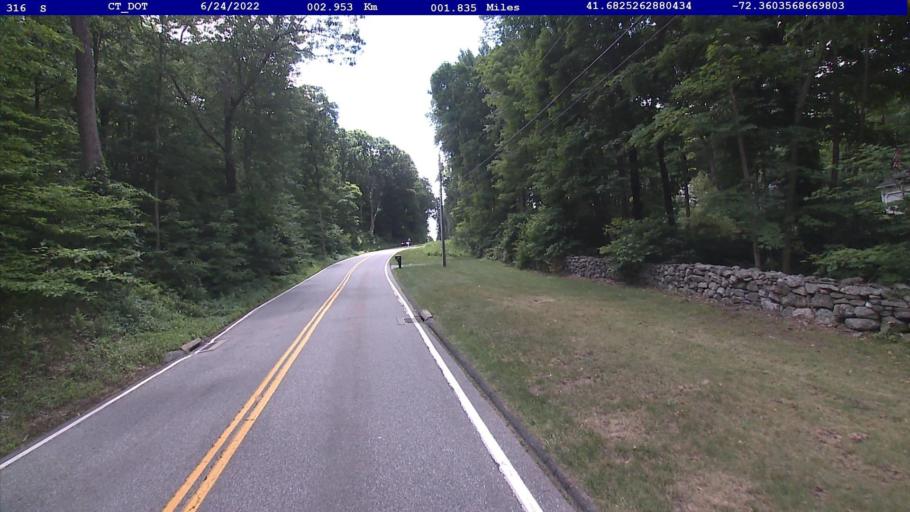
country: US
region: Connecticut
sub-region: Tolland County
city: Hebron
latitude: 41.6825
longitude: -72.3603
